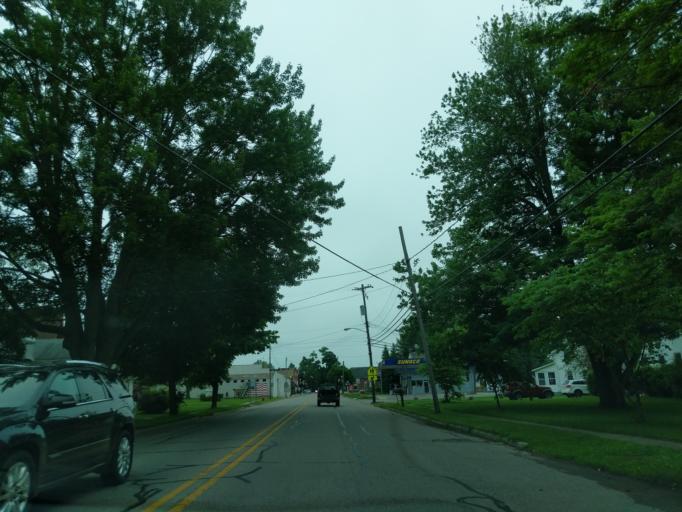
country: US
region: Michigan
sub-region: Hillsdale County
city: Litchfield
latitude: 42.0459
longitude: -84.7608
